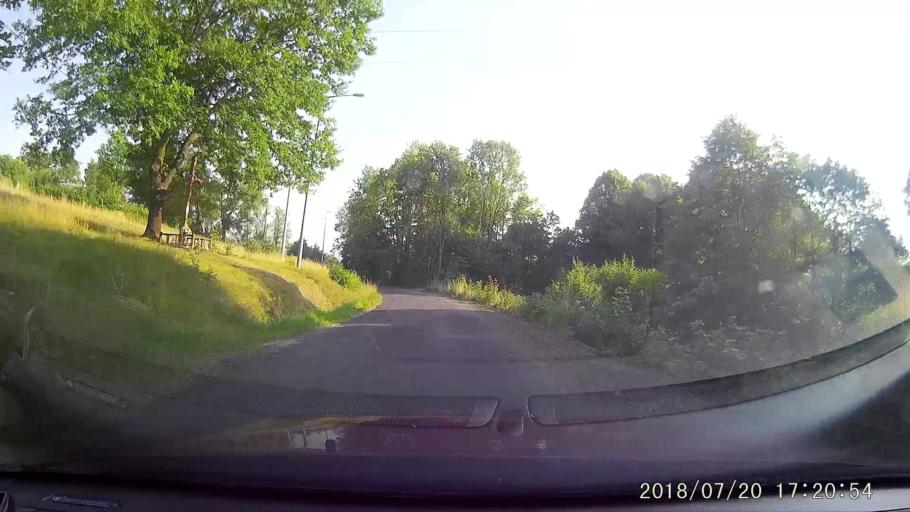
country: PL
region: Lower Silesian Voivodeship
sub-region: Powiat lubanski
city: Lesna
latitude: 50.9864
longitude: 15.2867
